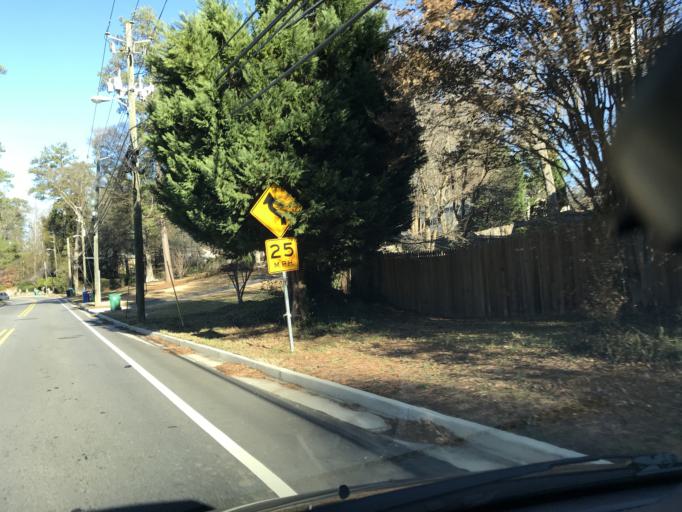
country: US
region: Georgia
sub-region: DeKalb County
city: North Atlanta
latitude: 33.8670
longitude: -84.3389
